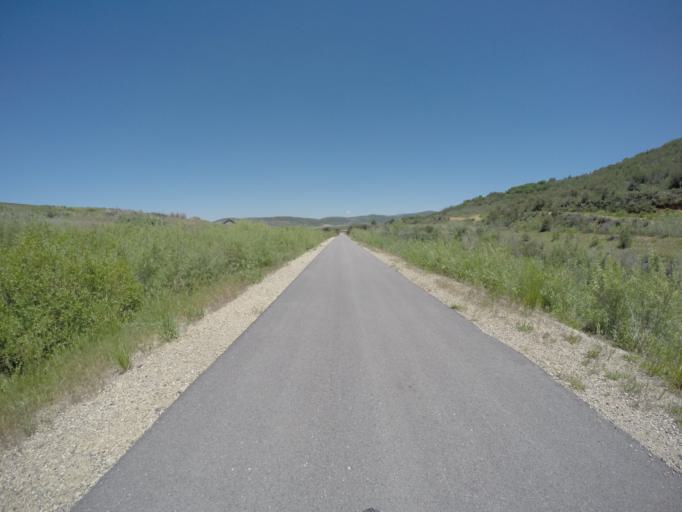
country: US
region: Utah
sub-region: Summit County
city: Park City
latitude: 40.6714
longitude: -111.4717
